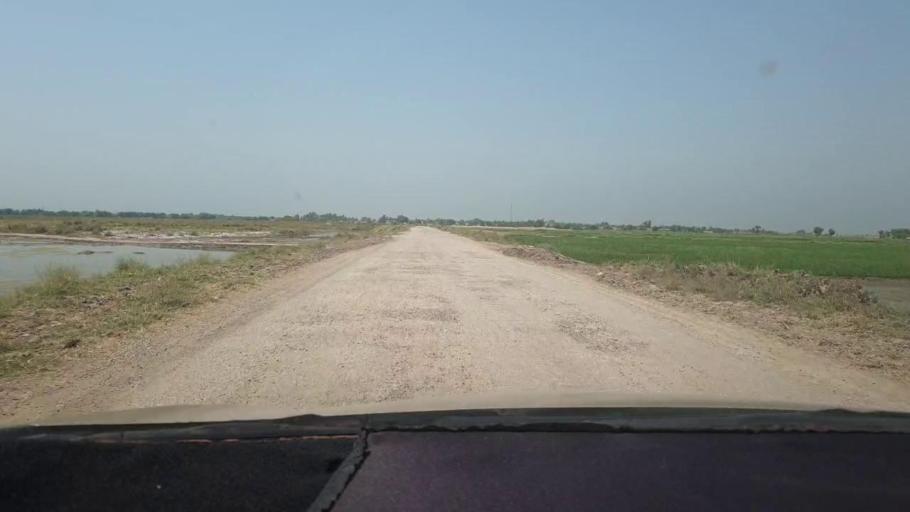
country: PK
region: Sindh
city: Miro Khan
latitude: 27.6636
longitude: 68.0723
